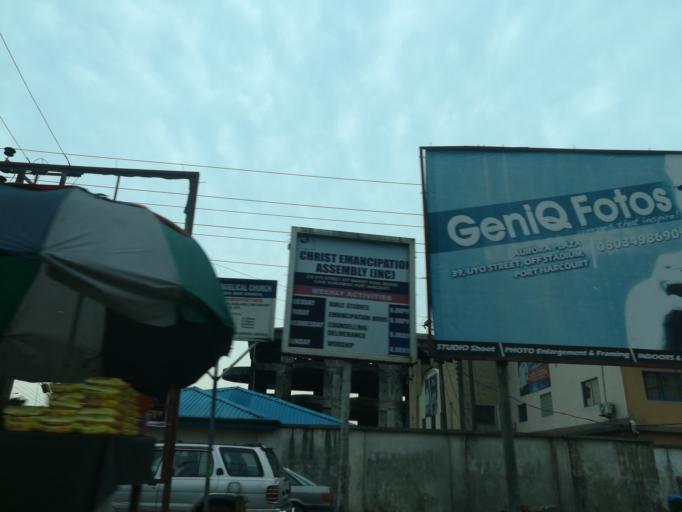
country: NG
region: Rivers
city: Port Harcourt
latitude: 4.8300
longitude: 7.0155
